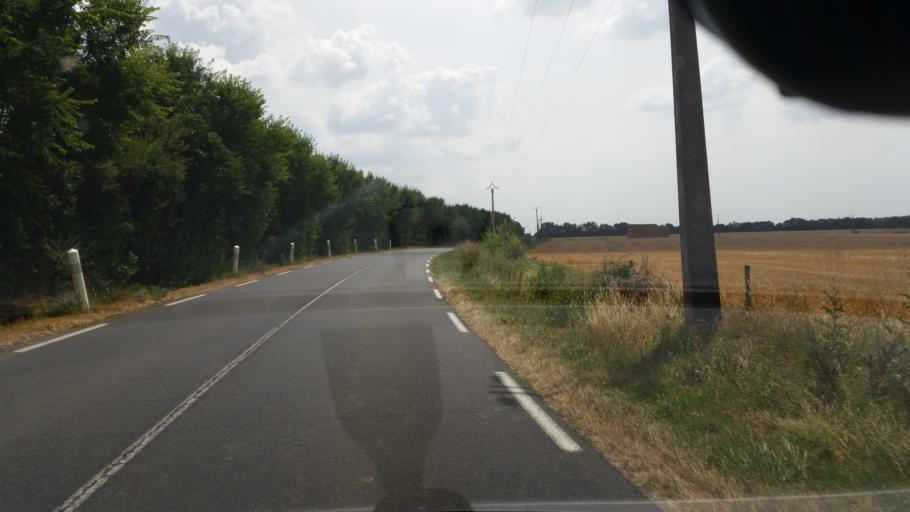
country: FR
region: Poitou-Charentes
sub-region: Departement de la Charente-Maritime
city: Courcon
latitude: 46.1625
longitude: -0.8287
